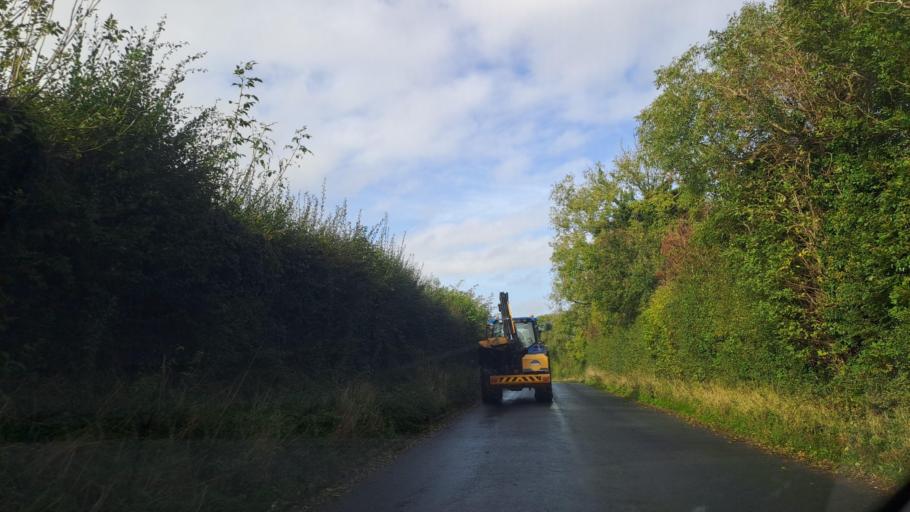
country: IE
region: Ulster
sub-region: County Monaghan
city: Carrickmacross
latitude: 53.8730
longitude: -6.6675
